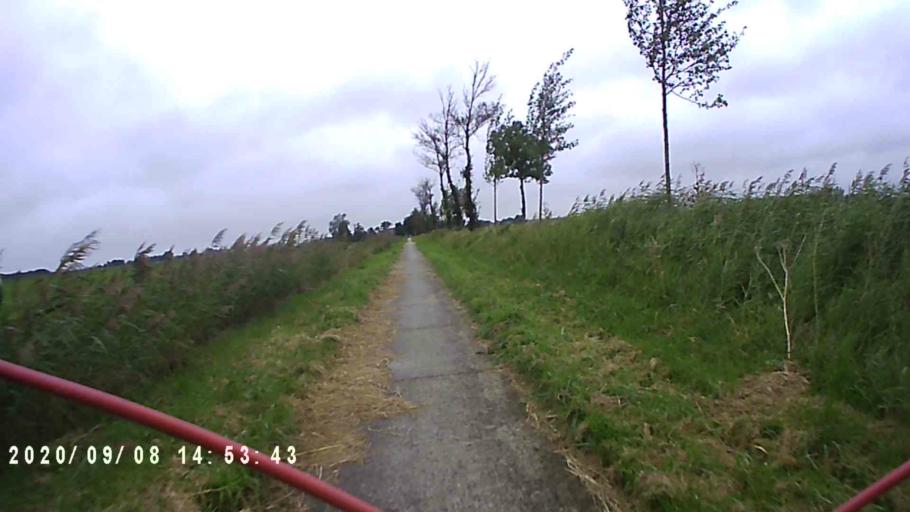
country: NL
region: Groningen
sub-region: Gemeente Slochteren
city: Slochteren
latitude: 53.2520
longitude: 6.7889
